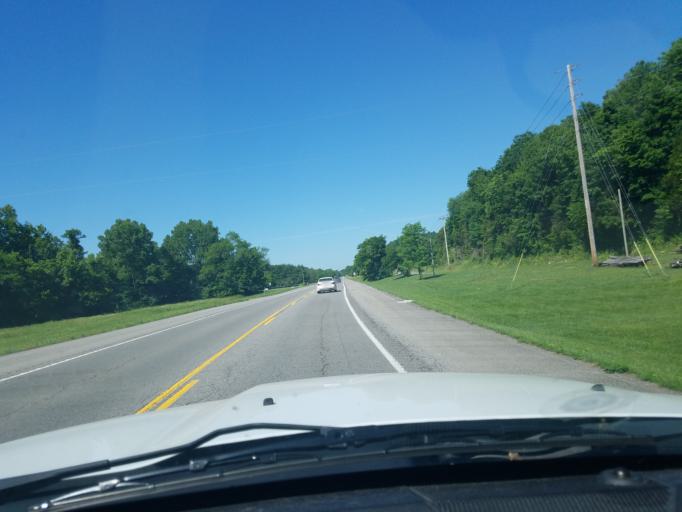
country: US
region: Tennessee
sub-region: Sumner County
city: Westmoreland
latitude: 36.5050
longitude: -86.2686
